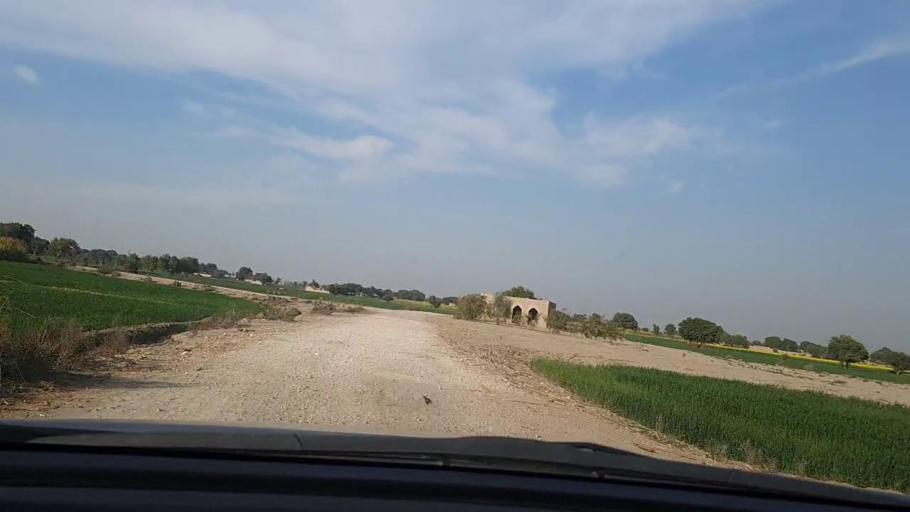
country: PK
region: Sindh
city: Daulatpur
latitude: 26.3274
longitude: 68.0264
